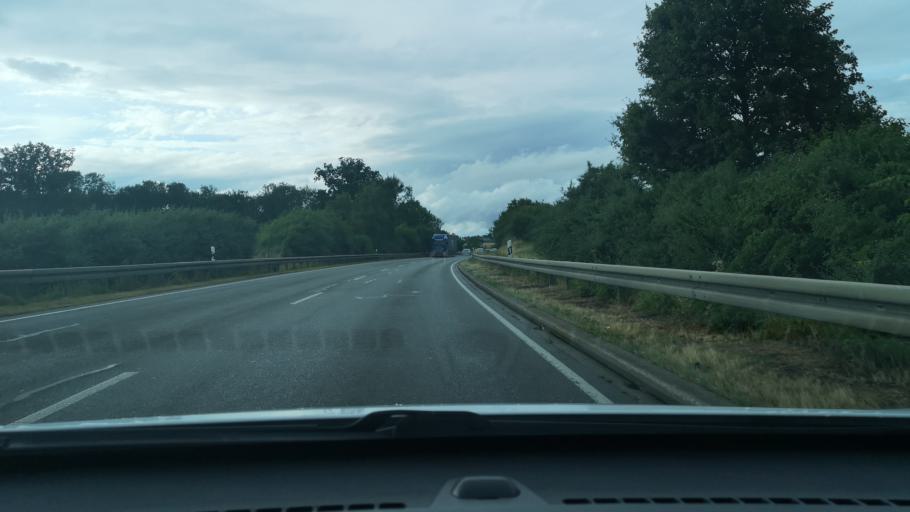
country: DE
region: Baden-Wuerttemberg
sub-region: Freiburg Region
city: Zimmern ob Rottweil
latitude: 48.1563
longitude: 8.6027
